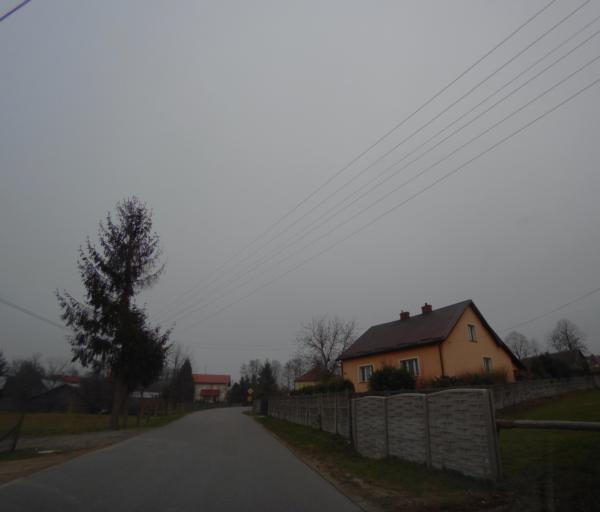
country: PL
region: Subcarpathian Voivodeship
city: Nowa Sarzyna
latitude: 50.2891
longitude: 22.3536
